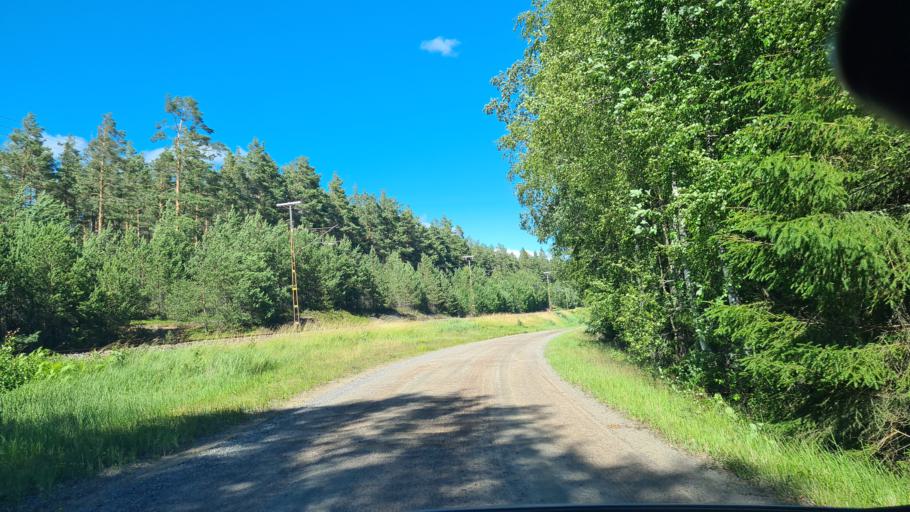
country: SE
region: OEstergoetland
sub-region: Norrkopings Kommun
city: Krokek
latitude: 58.7000
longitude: 16.4282
